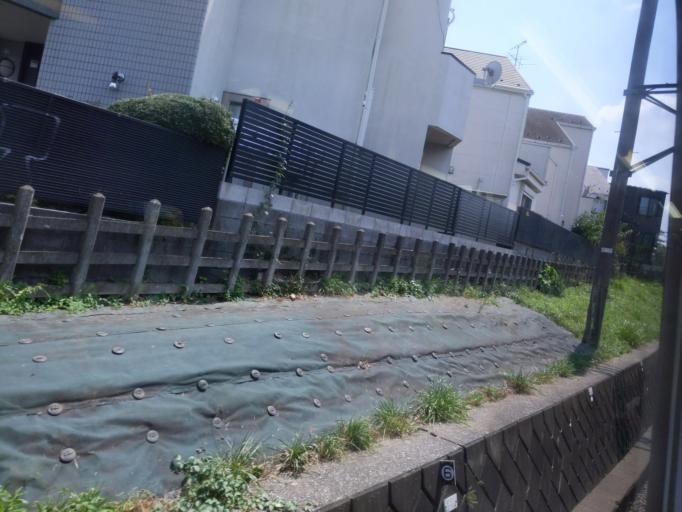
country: JP
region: Tokyo
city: Tokyo
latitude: 35.6026
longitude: 139.6686
